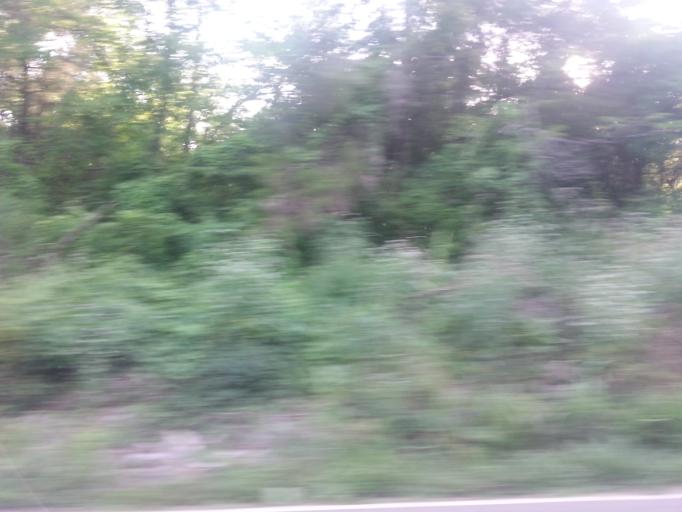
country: US
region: Tennessee
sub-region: Knox County
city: Knoxville
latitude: 35.9146
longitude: -83.9011
